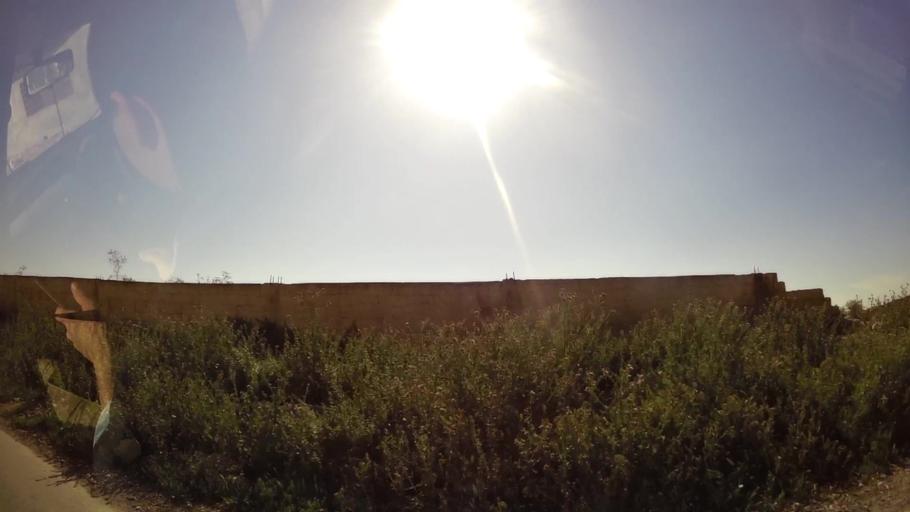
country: MA
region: Oriental
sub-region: Oujda-Angad
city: Oujda
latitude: 34.6893
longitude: -1.9228
